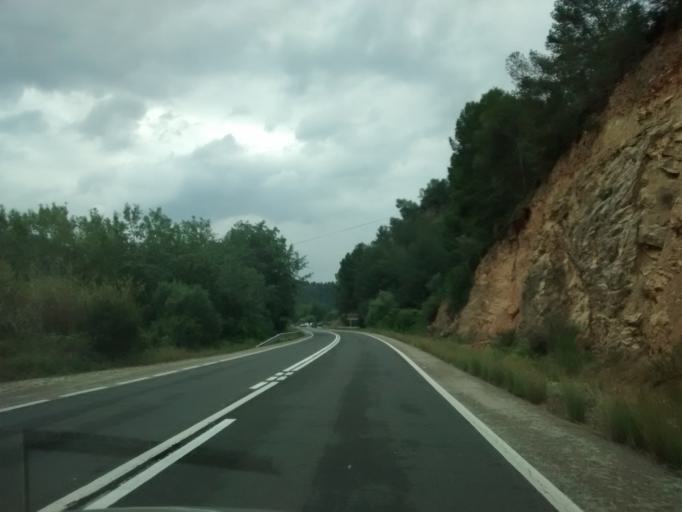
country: ES
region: Catalonia
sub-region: Provincia de Tarragona
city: Benifallet
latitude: 40.9676
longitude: 0.5097
